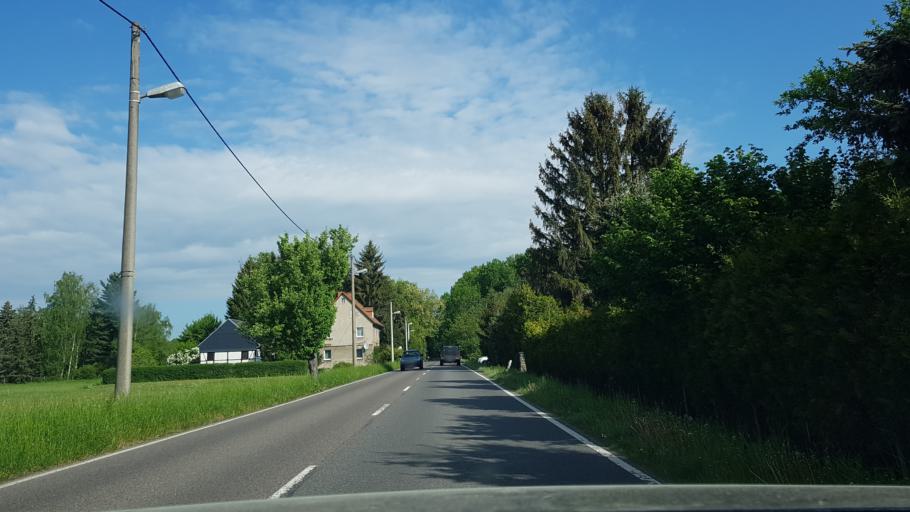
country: DE
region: Saxony
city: Wittgensdorf
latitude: 50.8847
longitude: 12.8965
